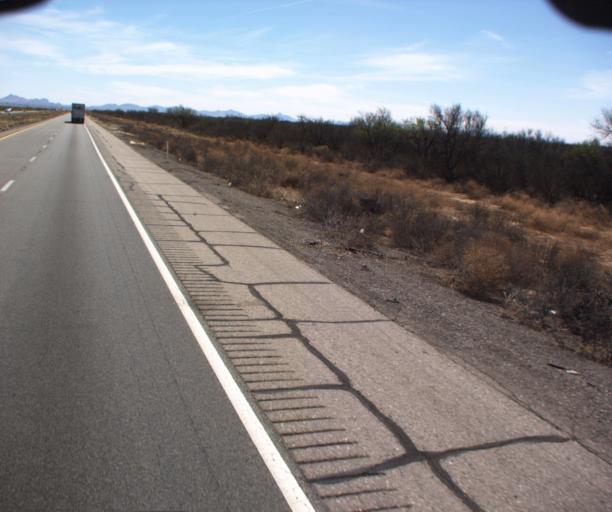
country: US
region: Arizona
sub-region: Cochise County
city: Willcox
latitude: 32.2896
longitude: -109.3210
